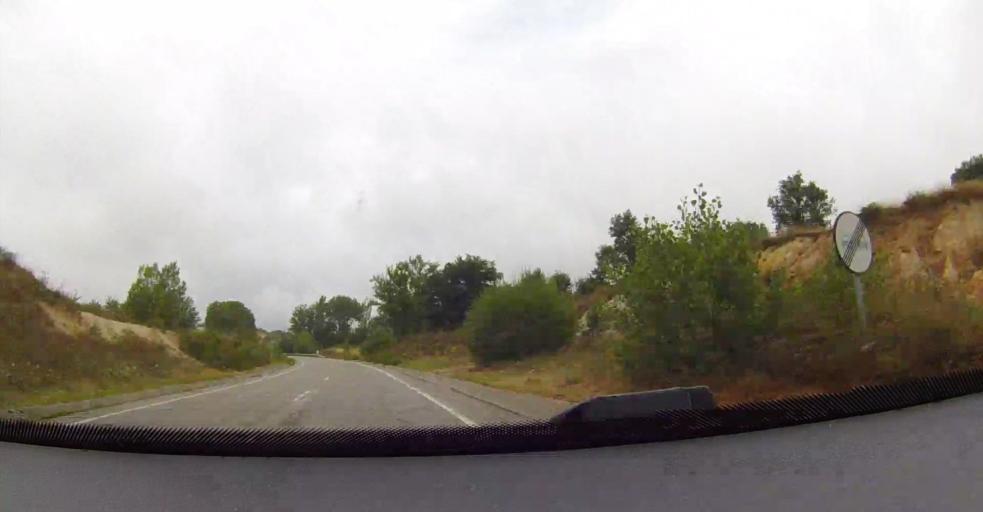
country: ES
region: Castille and Leon
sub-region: Provincia de Leon
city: Bonar
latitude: 42.8454
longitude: -5.2639
